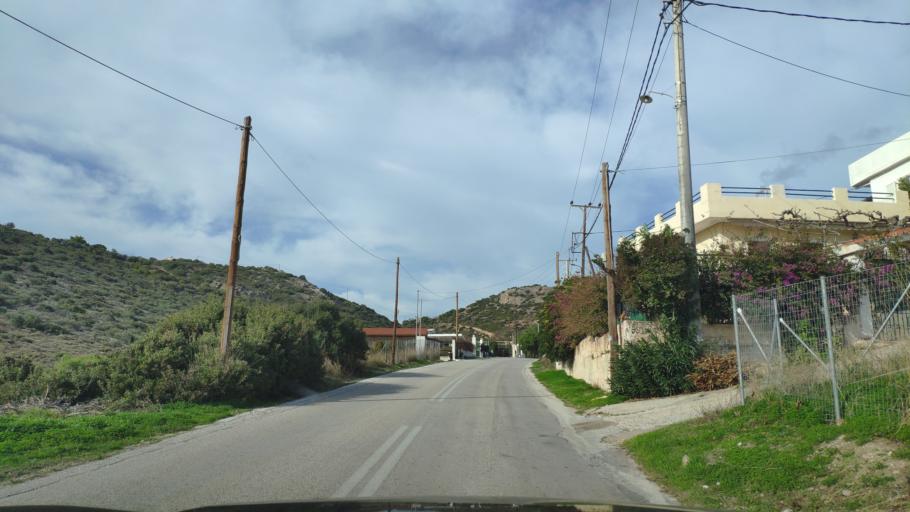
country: GR
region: Attica
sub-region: Nomarchia Anatolikis Attikis
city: Limin Mesoyaias
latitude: 37.9007
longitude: 24.0231
